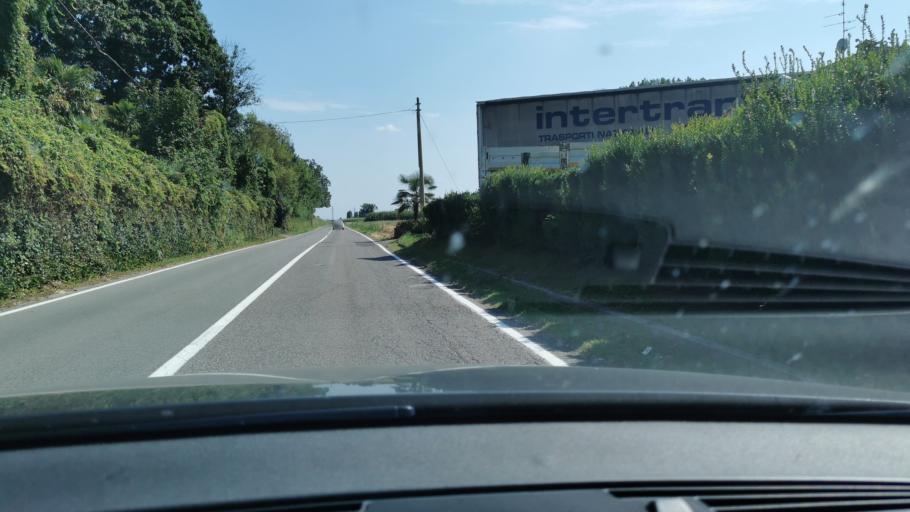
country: IT
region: Lombardy
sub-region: Provincia di Como
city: Fenegro
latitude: 45.6950
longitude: 8.9961
